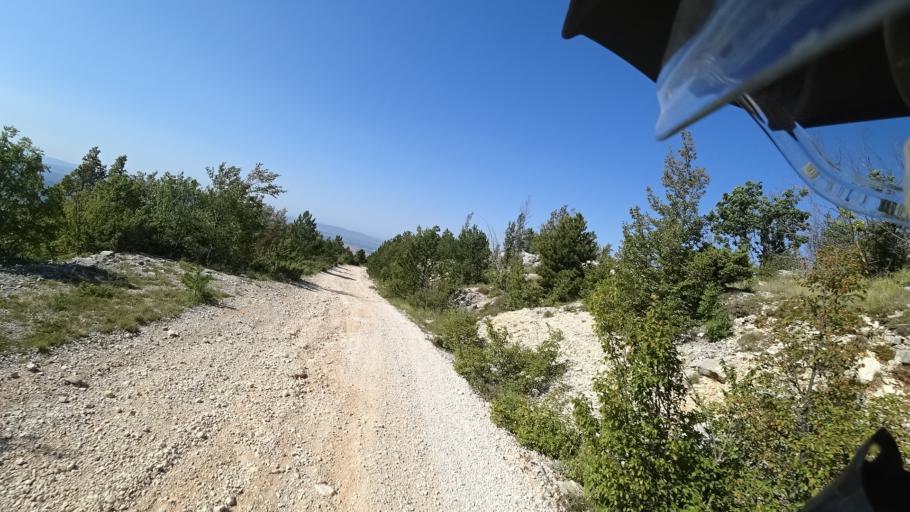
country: HR
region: Sibensko-Kniniska
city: Drnis
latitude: 43.9152
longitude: 16.1698
